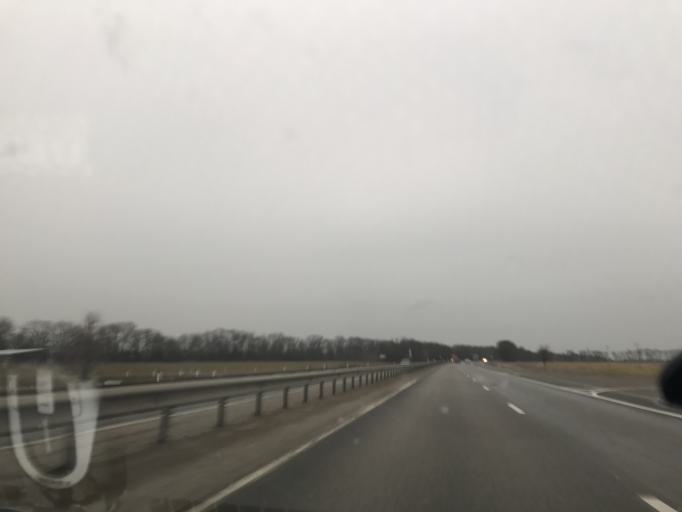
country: RU
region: Krasnodarskiy
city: Pavlovskaya
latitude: 46.1824
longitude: 39.8339
